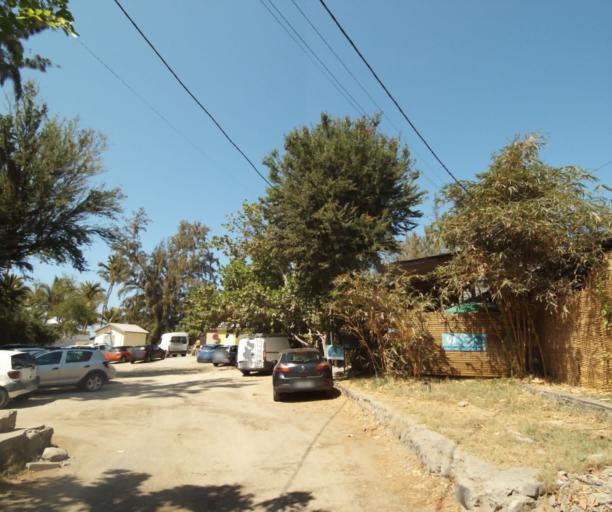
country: RE
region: Reunion
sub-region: Reunion
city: Trois-Bassins
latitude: -21.0993
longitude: 55.2424
